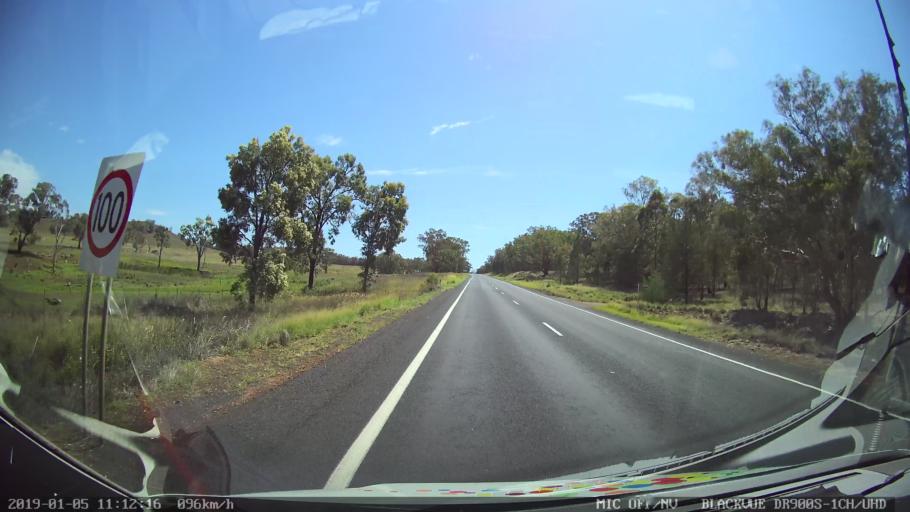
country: AU
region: New South Wales
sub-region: Warrumbungle Shire
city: Coonabarabran
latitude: -31.3838
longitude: 149.2588
